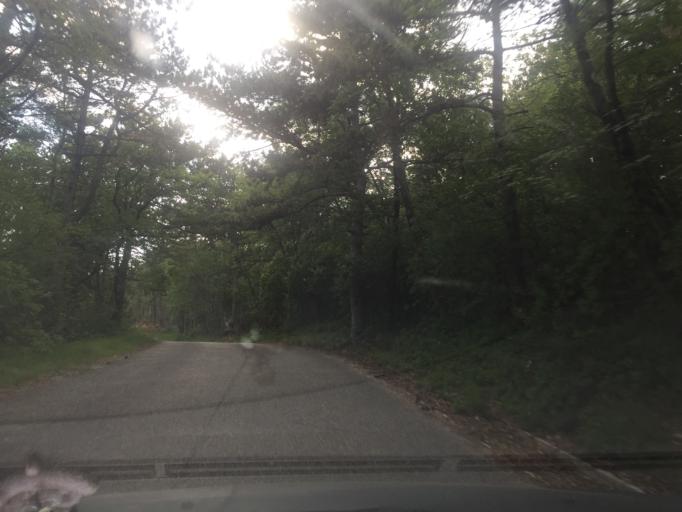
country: IT
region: Friuli Venezia Giulia
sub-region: Provincia di Gorizia
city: Doberdo del Lago
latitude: 45.8755
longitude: 13.5502
